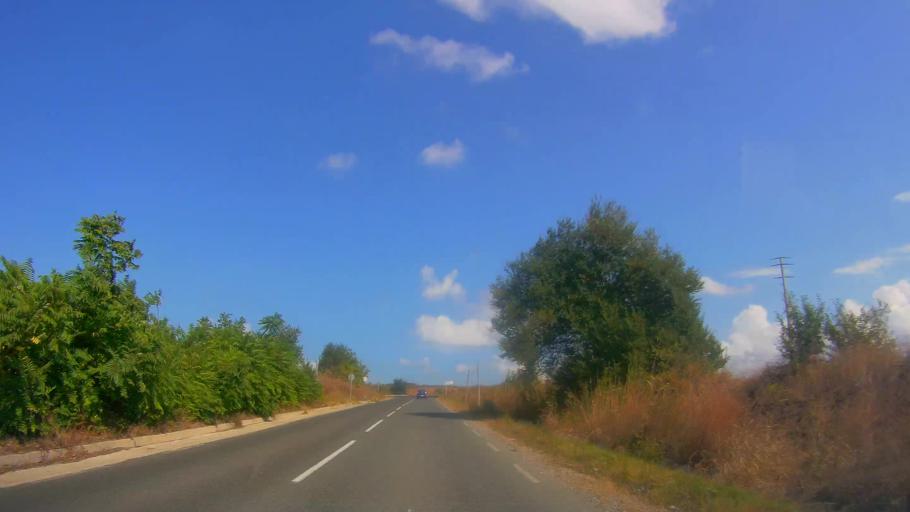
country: BG
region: Burgas
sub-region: Obshtina Burgas
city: Burgas
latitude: 42.4809
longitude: 27.3843
